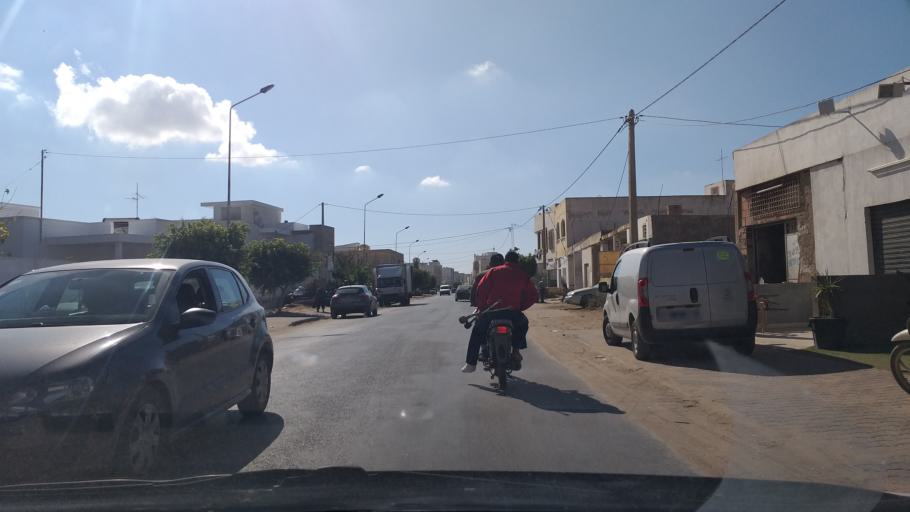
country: TN
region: Safaqis
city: Al Qarmadah
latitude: 34.8024
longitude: 10.7812
